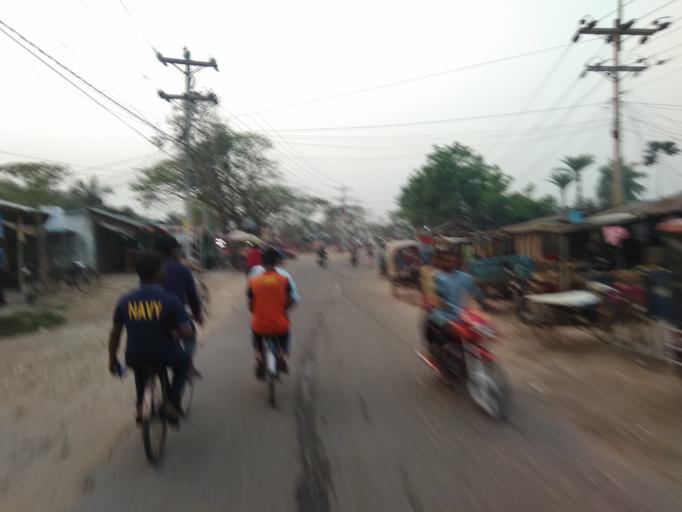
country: IN
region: West Bengal
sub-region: North 24 Parganas
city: Taki
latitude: 22.4536
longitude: 89.0348
